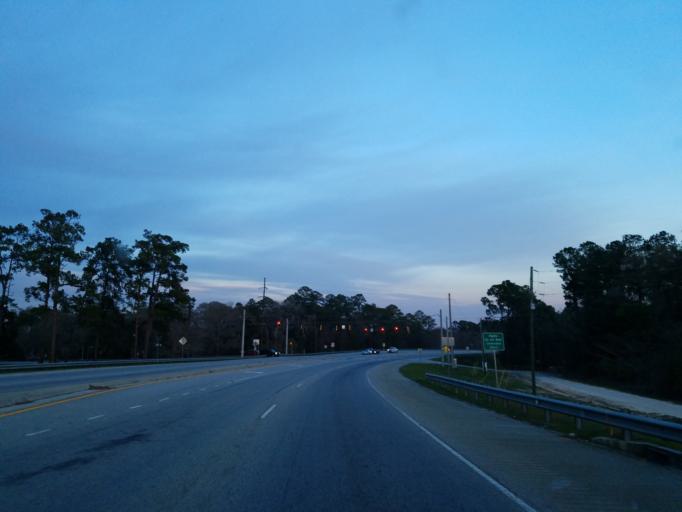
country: US
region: Georgia
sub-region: Lowndes County
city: Remerton
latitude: 30.8529
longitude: -83.3459
